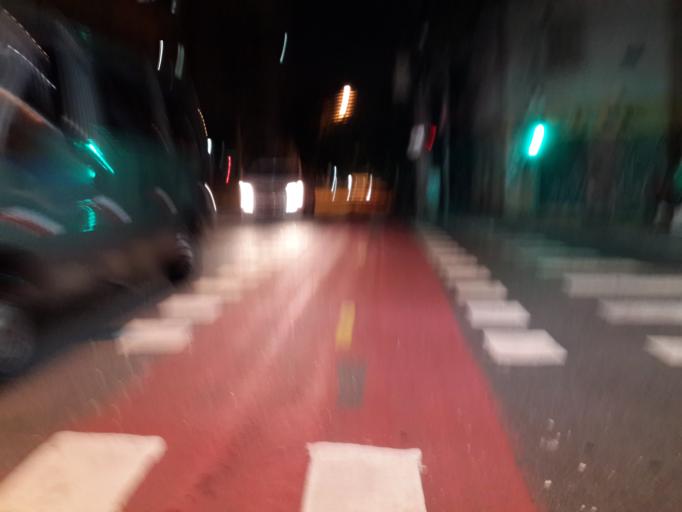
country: BR
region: Sao Paulo
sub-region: Sao Paulo
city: Sao Paulo
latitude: -23.5667
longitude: -46.6882
